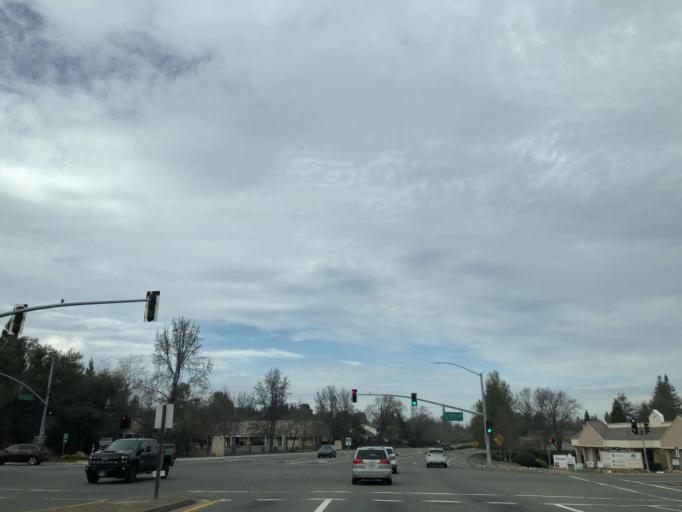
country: US
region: California
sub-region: El Dorado County
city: El Dorado Hills
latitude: 38.6862
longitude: -121.0795
